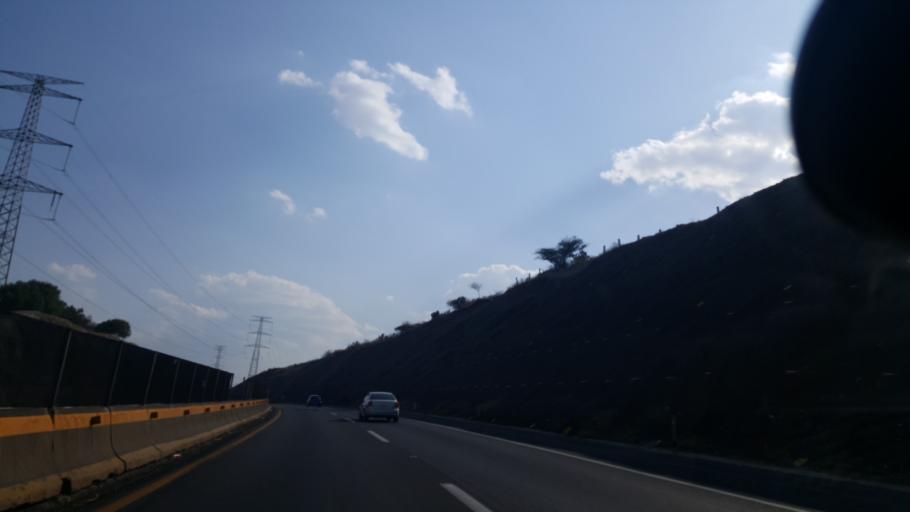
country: MX
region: Mexico
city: Ciudad Lopez Mateos
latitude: 19.5571
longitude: -99.2775
